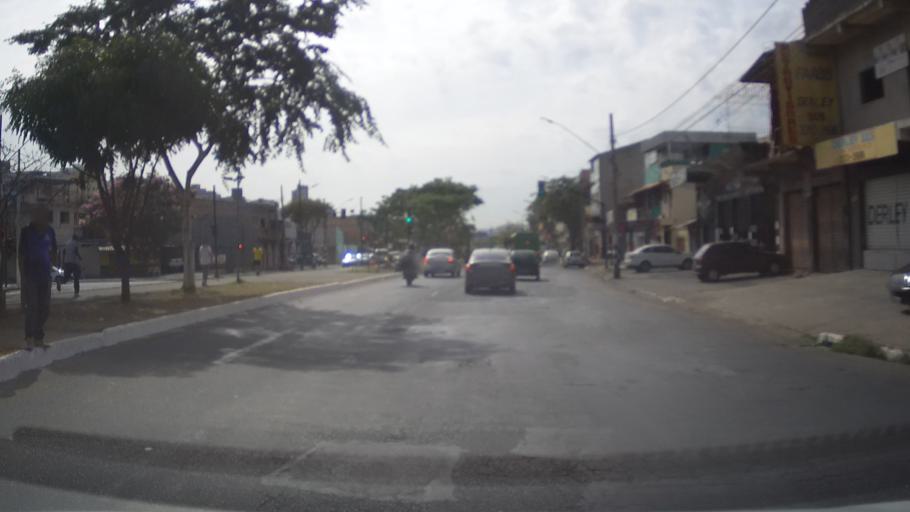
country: BR
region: Minas Gerais
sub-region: Contagem
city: Contagem
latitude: -19.9457
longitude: -44.0484
